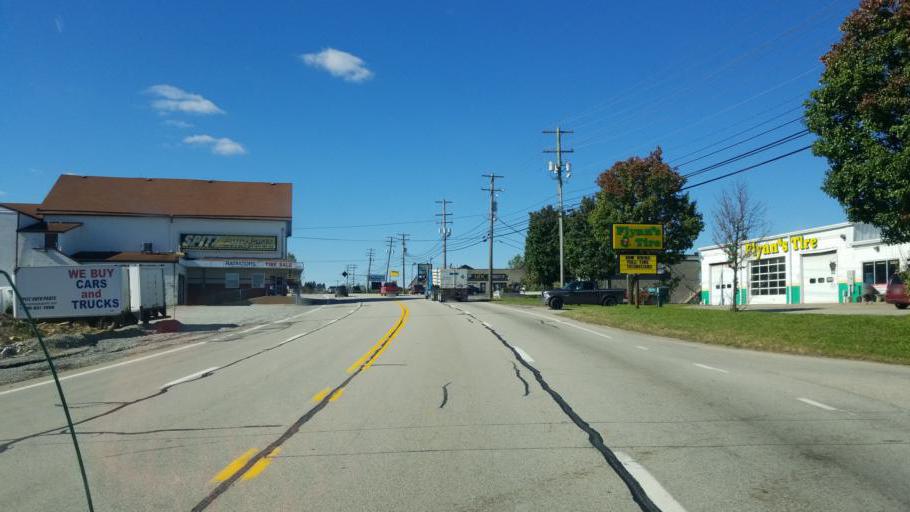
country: US
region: Pennsylvania
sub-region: Westmoreland County
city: Irwin
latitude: 40.3371
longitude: -79.7462
